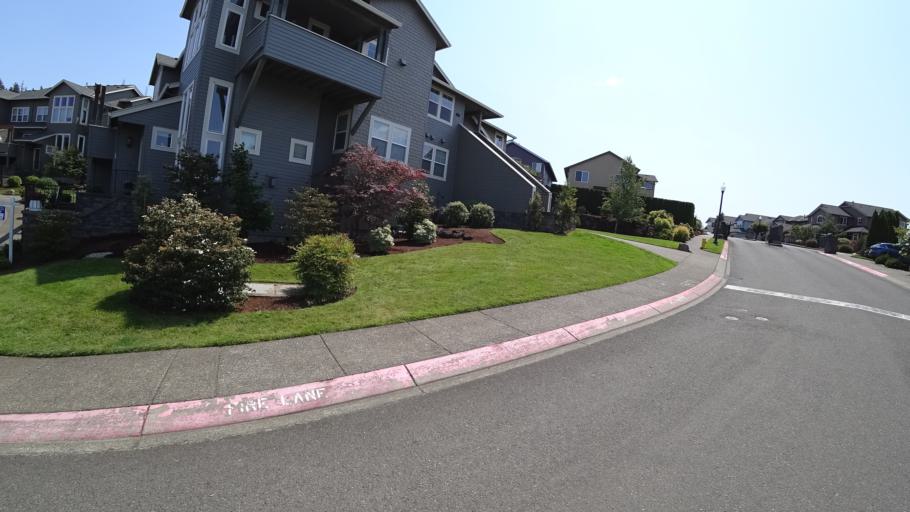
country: US
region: Oregon
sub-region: Multnomah County
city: Lents
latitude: 45.4589
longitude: -122.5583
